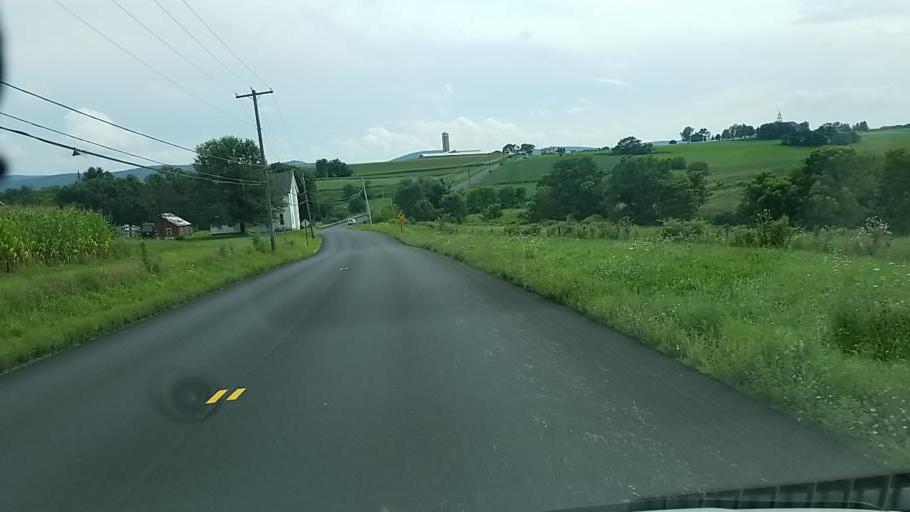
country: US
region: Pennsylvania
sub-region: Dauphin County
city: Elizabethville
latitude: 40.5944
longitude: -76.8097
